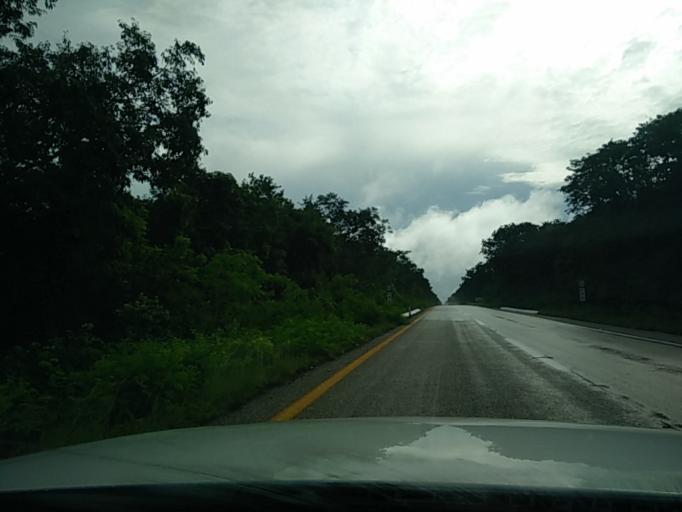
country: MX
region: Yucatan
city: Tunkas
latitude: 20.7605
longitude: -88.7766
